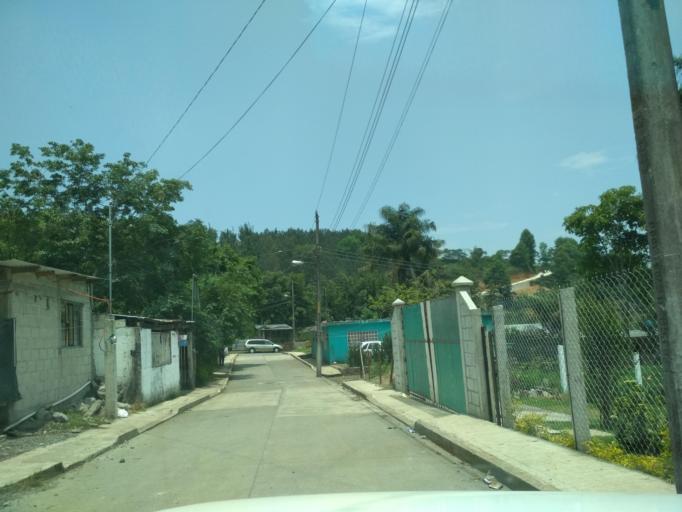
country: MX
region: Veracruz
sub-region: Mariano Escobedo
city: Mariano Escobedo
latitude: 18.9122
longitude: -97.1263
